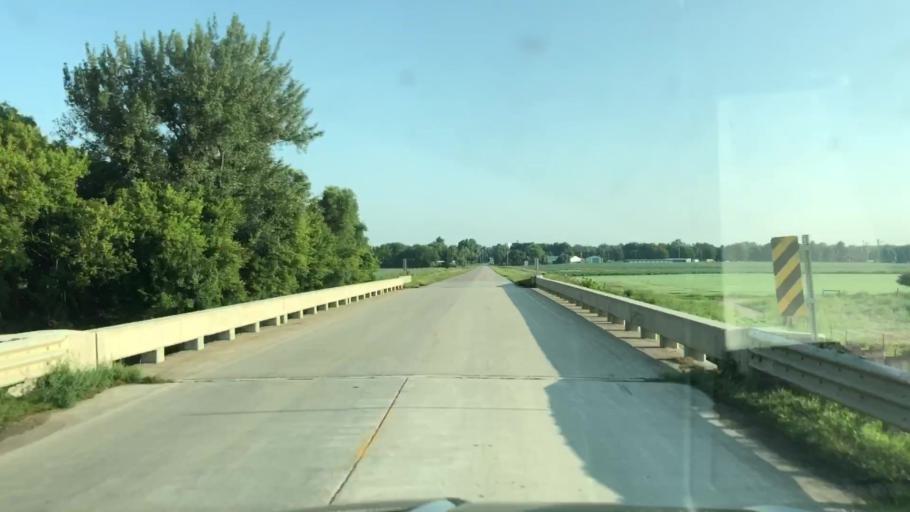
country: US
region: Iowa
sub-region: Lyon County
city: George
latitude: 43.3328
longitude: -95.9987
